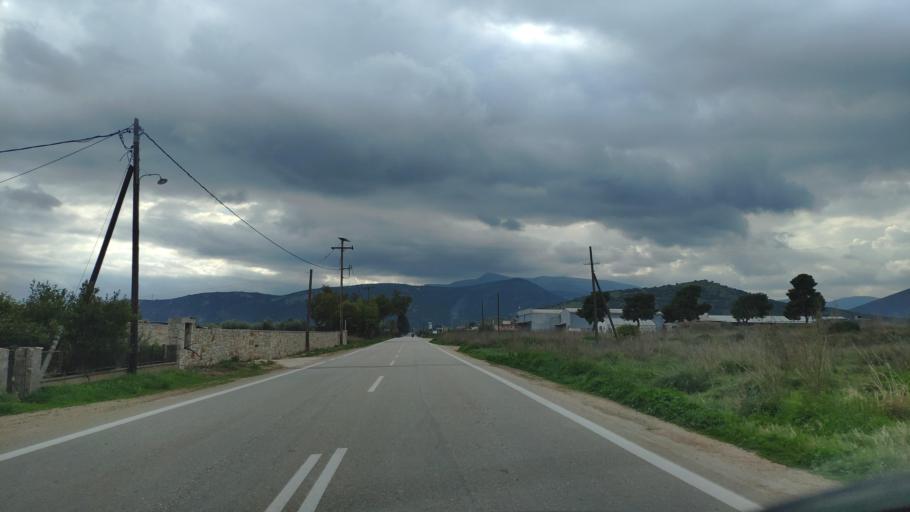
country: GR
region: Peloponnese
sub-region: Nomos Argolidos
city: Nea Kios
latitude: 37.5498
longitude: 22.7169
